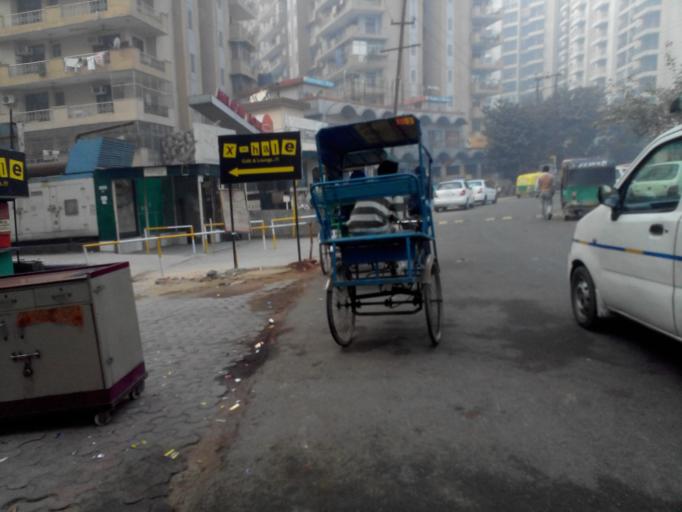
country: IN
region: Uttar Pradesh
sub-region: Gautam Buddha Nagar
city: Noida
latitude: 28.6364
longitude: 77.3636
